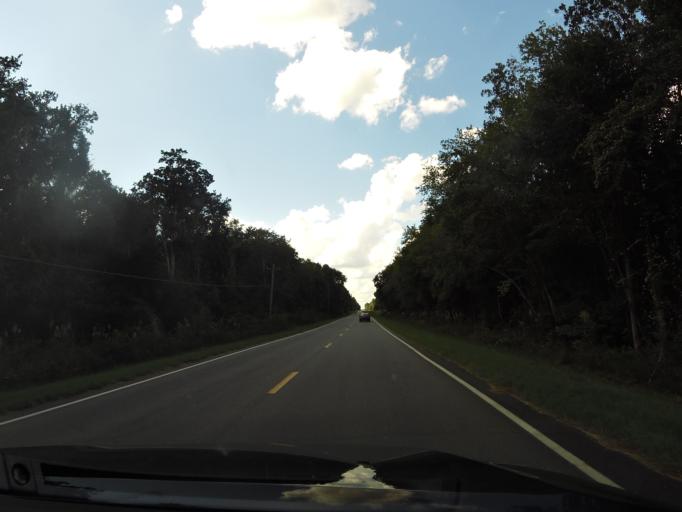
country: US
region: Georgia
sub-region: Lowndes County
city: Valdosta
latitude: 30.7791
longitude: -83.1557
